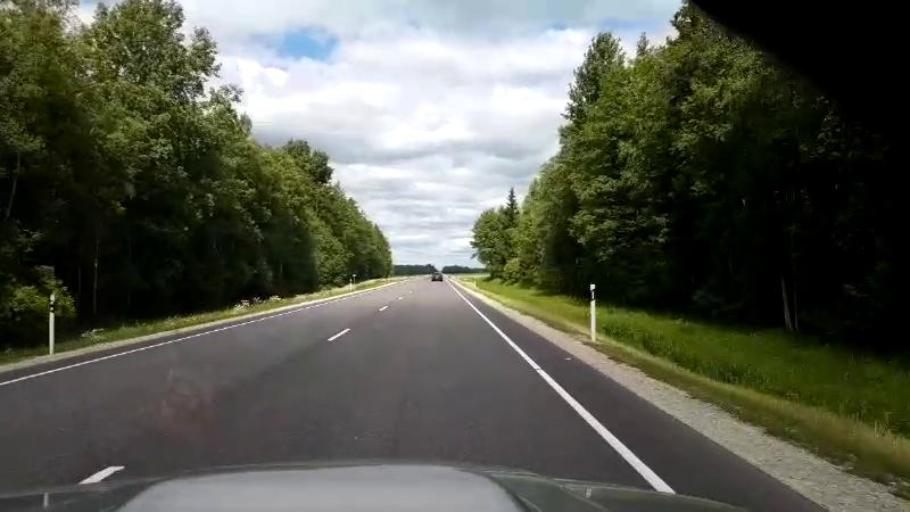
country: EE
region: Raplamaa
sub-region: Maerjamaa vald
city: Marjamaa
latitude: 58.8403
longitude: 24.4240
